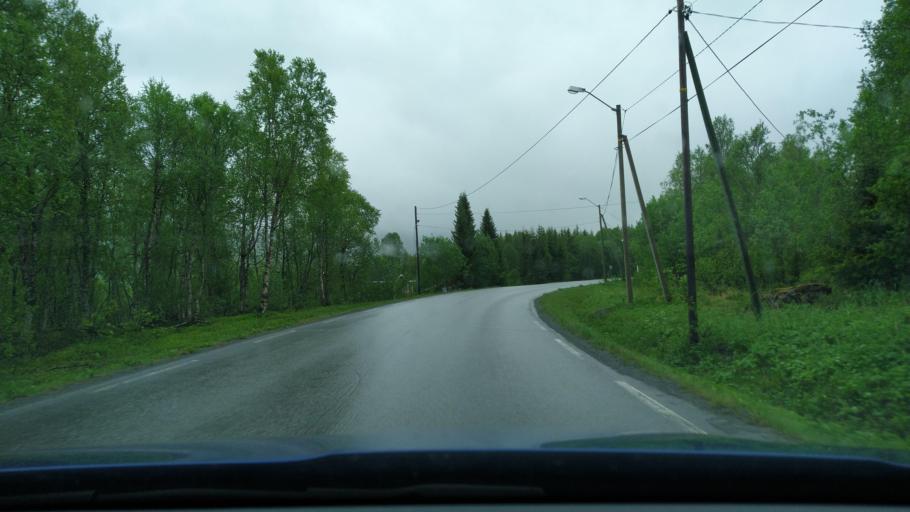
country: NO
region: Troms
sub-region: Dyroy
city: Brostadbotn
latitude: 69.0483
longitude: 17.7317
